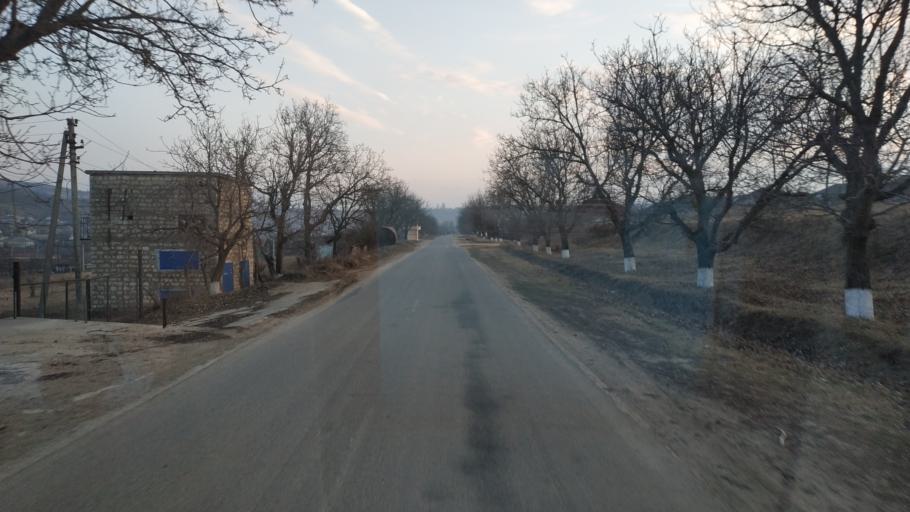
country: MD
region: Hincesti
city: Dancu
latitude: 46.6787
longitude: 28.3352
